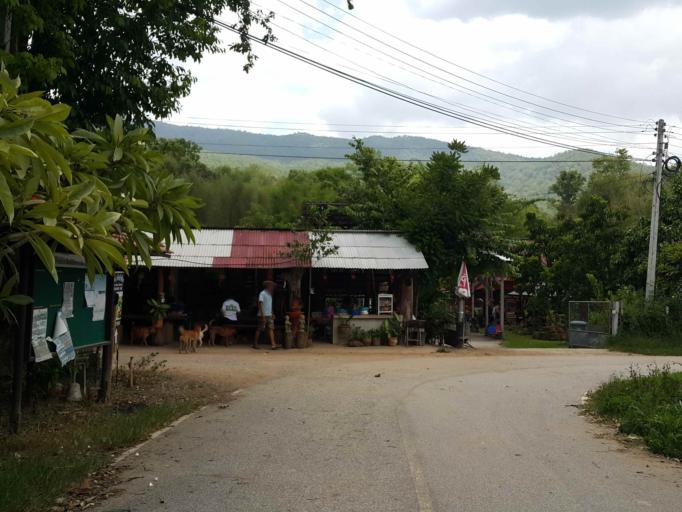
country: TH
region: Chiang Mai
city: Hang Dong
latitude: 18.7622
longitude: 98.9064
